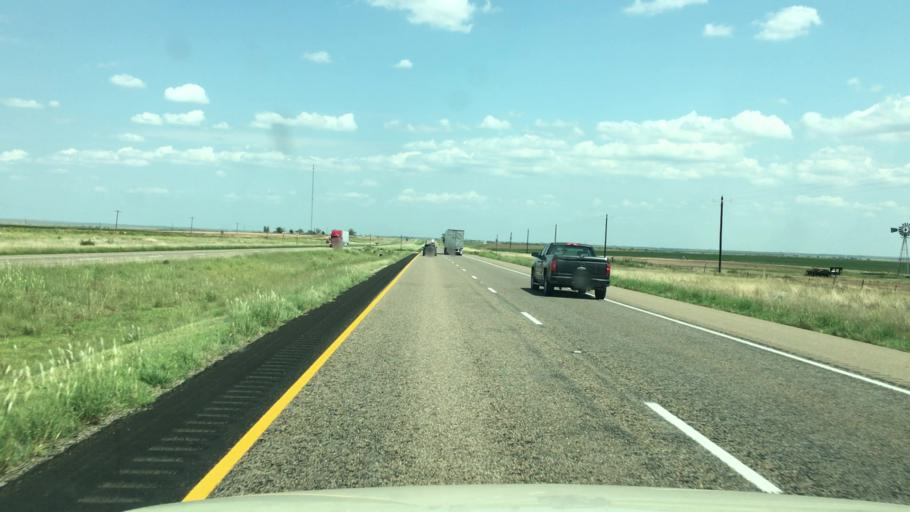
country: US
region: Texas
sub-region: Armstrong County
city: Claude
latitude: 35.0332
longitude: -101.1620
